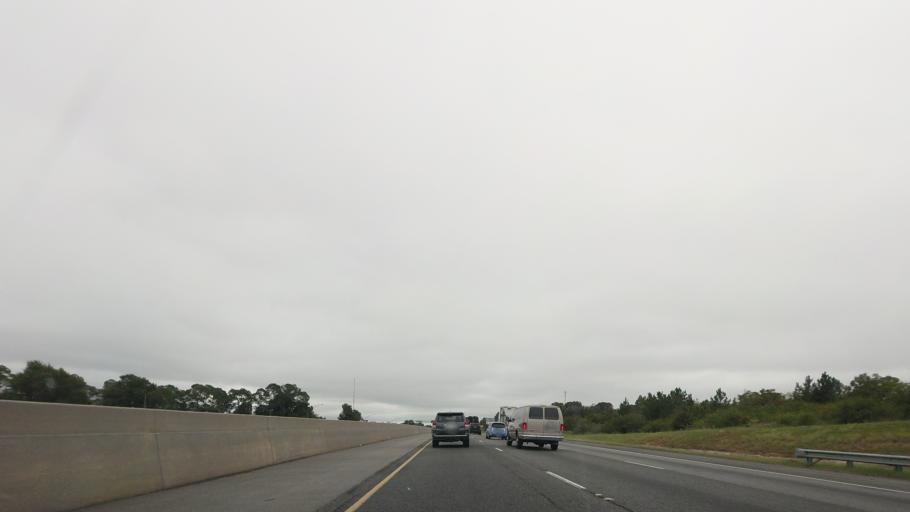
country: US
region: Georgia
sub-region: Turner County
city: Ashburn
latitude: 31.7502
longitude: -83.6628
